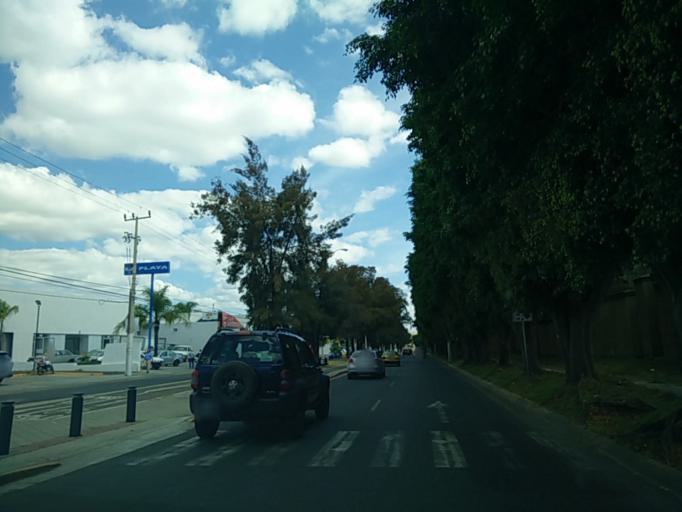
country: MX
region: Jalisco
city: Nuevo Mexico
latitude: 20.7297
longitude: -103.4387
